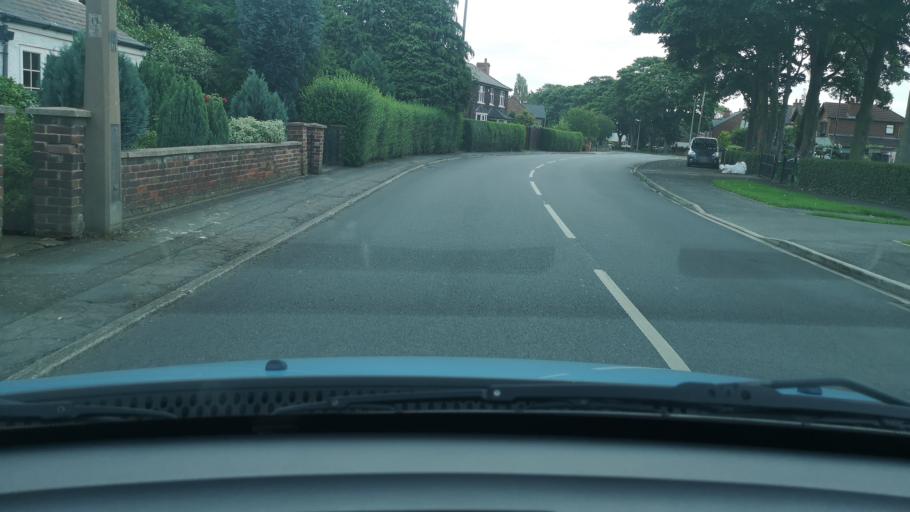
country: GB
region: England
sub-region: North Lincolnshire
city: Scunthorpe
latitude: 53.5846
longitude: -0.6593
